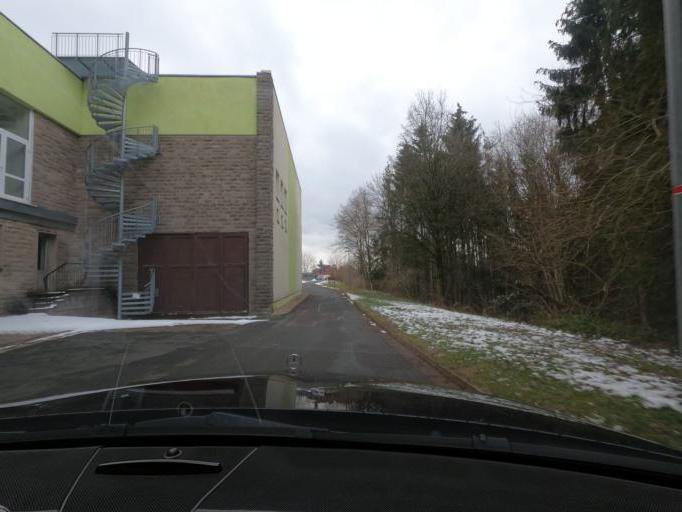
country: DE
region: Thuringia
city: Finsterbergen
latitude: 50.8312
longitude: 10.5883
